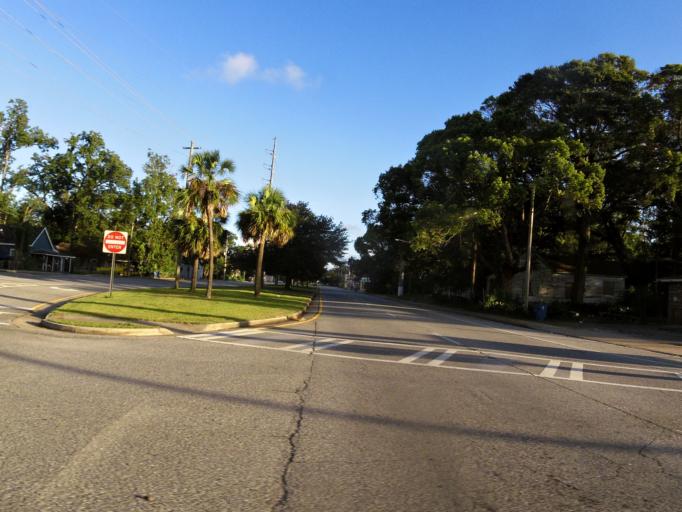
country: US
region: Georgia
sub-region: Glynn County
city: Brunswick
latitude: 31.1537
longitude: -81.4891
